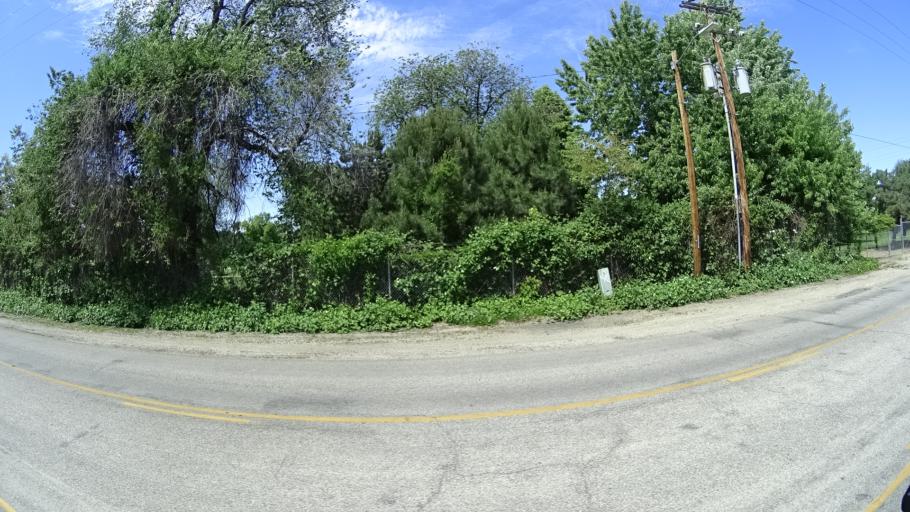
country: US
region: Idaho
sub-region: Ada County
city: Garden City
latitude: 43.5883
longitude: -116.2336
